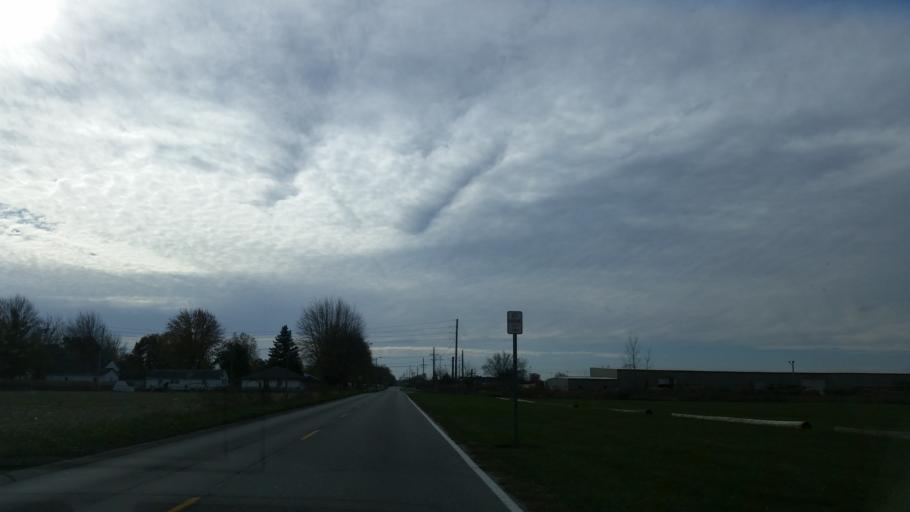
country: US
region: Indiana
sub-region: Howard County
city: Kokomo
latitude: 40.4668
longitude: -86.1555
